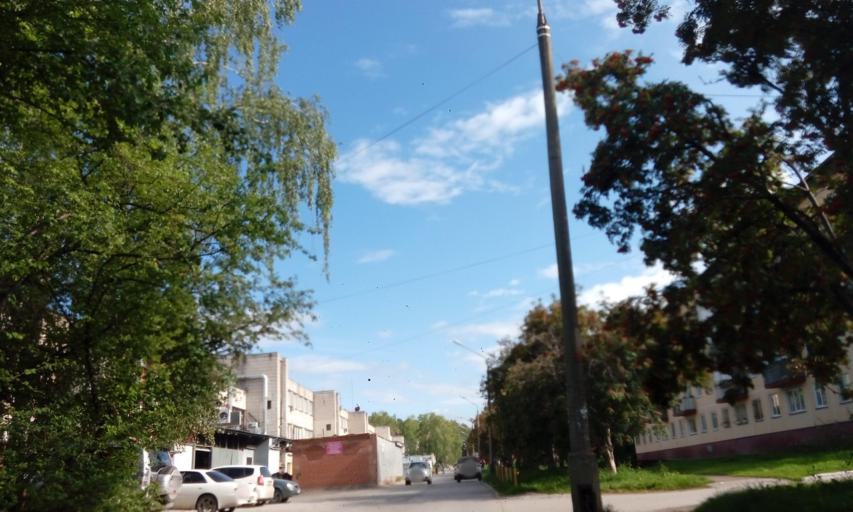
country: RU
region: Novosibirsk
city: Akademgorodok
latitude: 54.8404
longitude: 83.0932
